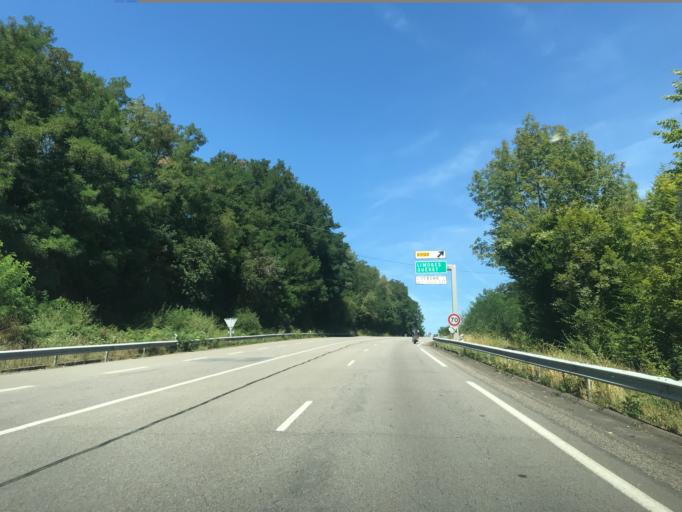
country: FR
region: Limousin
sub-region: Departement de la Correze
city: Tulle
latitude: 45.2706
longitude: 1.7899
